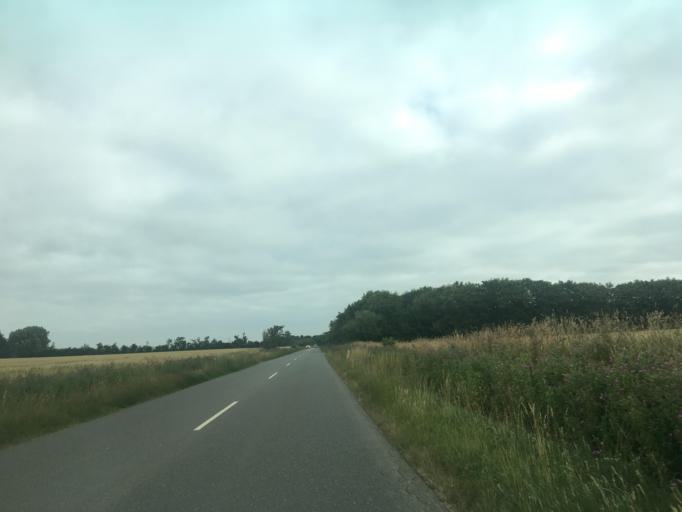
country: DK
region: North Denmark
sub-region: Thisted Kommune
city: Thisted
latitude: 56.8408
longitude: 8.5854
